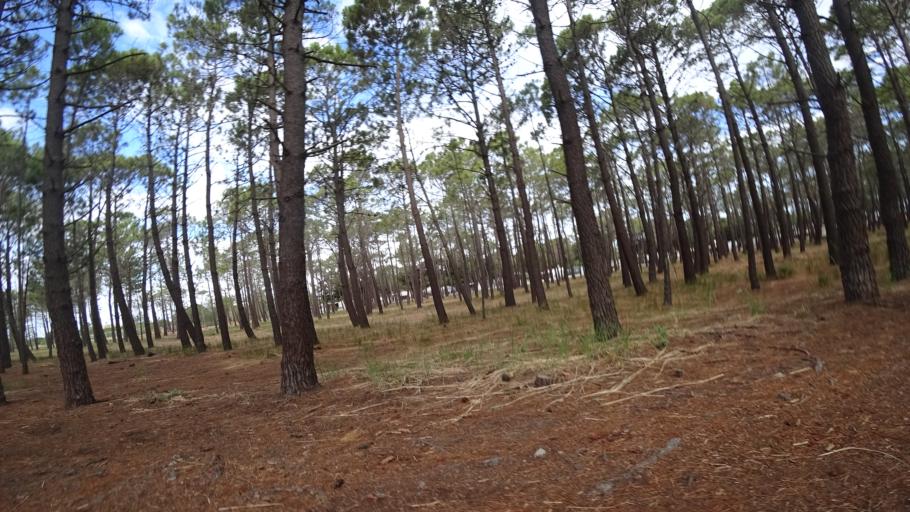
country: FR
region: Languedoc-Roussillon
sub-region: Departement des Pyrenees-Orientales
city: Le Barcares
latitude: 42.8202
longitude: 3.0342
